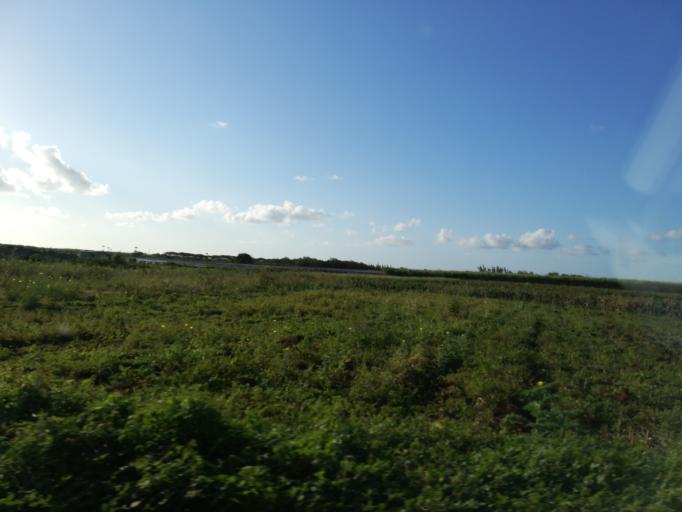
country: MU
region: Pamplemousses
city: Morcellemont Saint Andre
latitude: -20.0796
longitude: 57.5363
